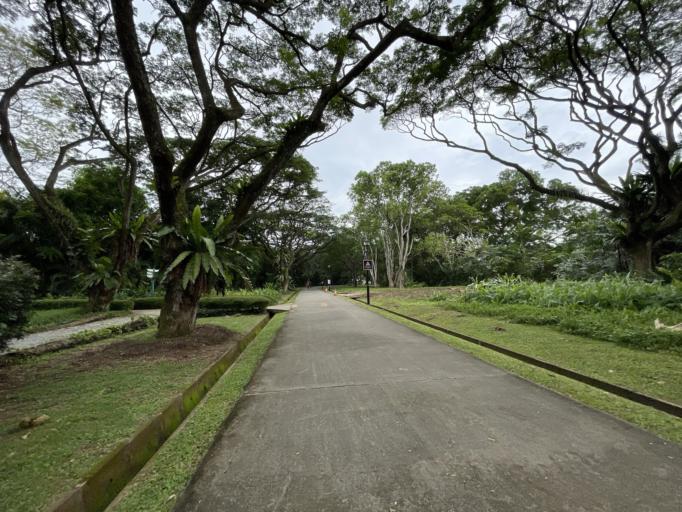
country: SG
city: Singapore
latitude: 1.2887
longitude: 103.7736
